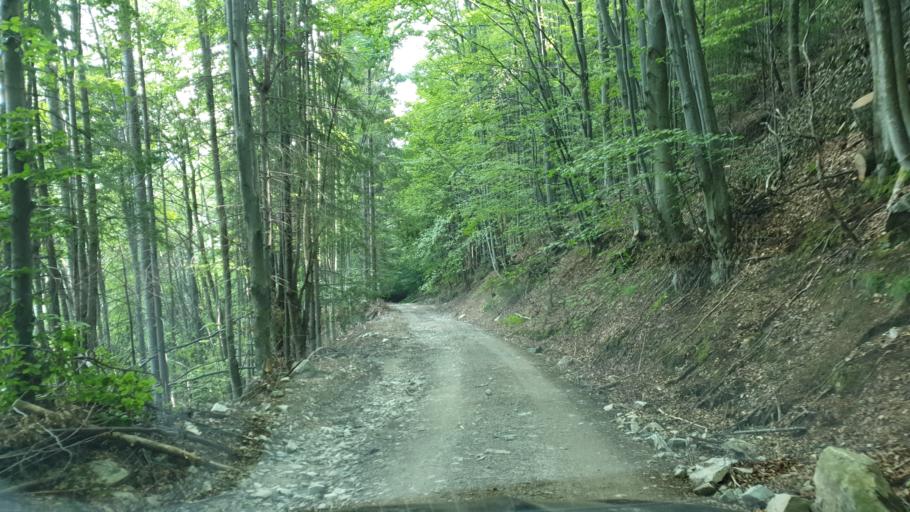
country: RO
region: Hunedoara
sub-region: Comuna Uricani
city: Uricani
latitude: 45.3091
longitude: 22.9812
